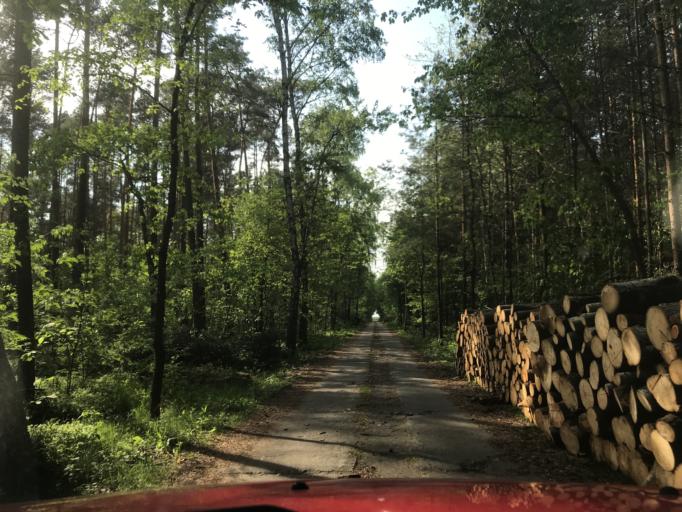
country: PL
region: Greater Poland Voivodeship
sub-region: Powiat kaliski
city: Stawiszyn
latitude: 51.9405
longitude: 18.1563
